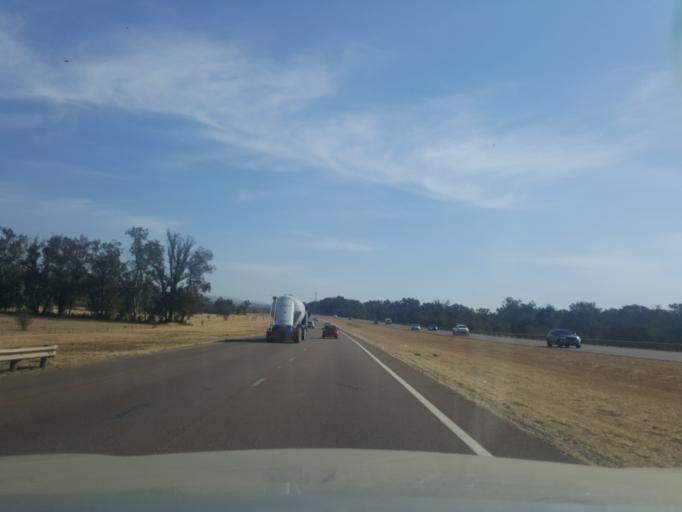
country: ZA
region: Gauteng
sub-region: City of Tshwane Metropolitan Municipality
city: Pretoria
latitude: -25.6381
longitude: 28.1959
